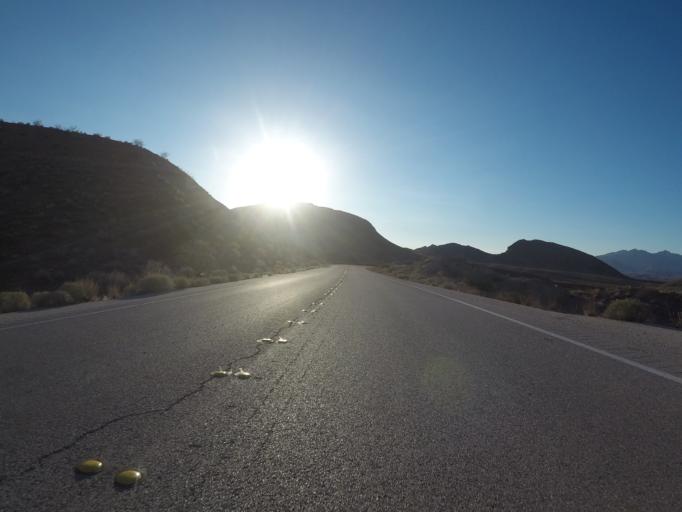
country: US
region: Nevada
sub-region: Clark County
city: Moapa Valley
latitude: 36.2433
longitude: -114.5381
